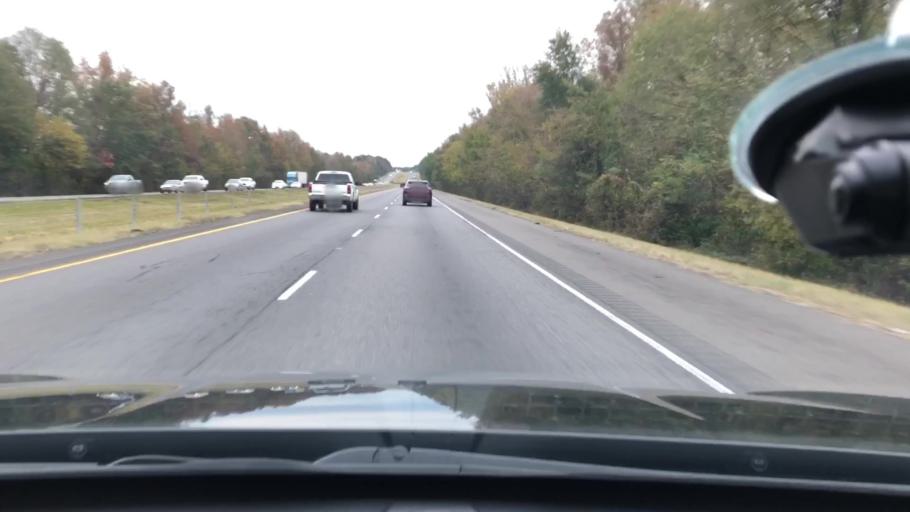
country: US
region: Arkansas
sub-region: Clark County
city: Gurdon
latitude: 34.0226
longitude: -93.1570
